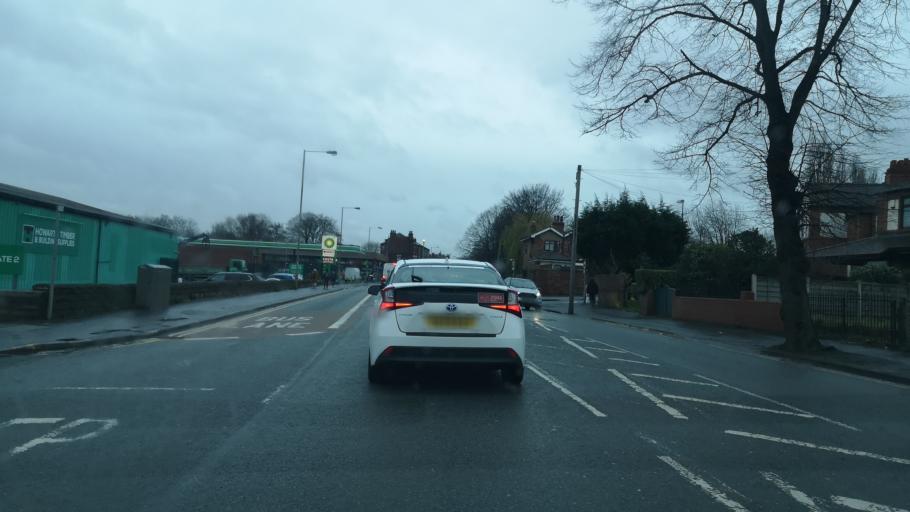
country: GB
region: England
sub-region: City and Borough of Wakefield
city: Wakefield
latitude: 53.6734
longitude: -1.4865
